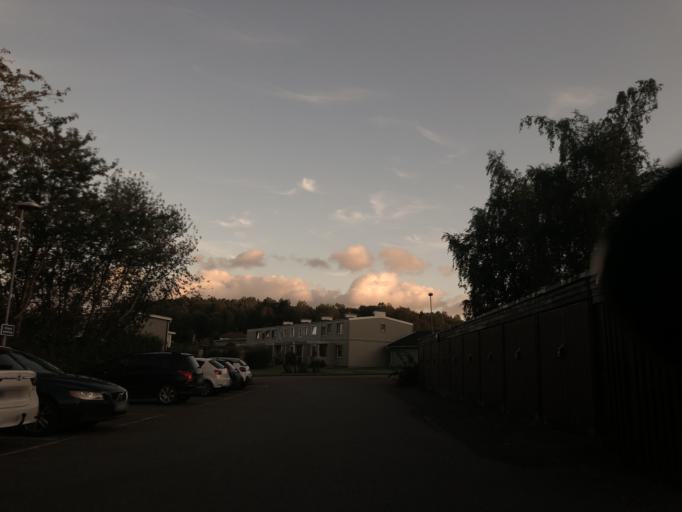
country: SE
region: Vaestra Goetaland
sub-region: Goteborg
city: Goeteborg
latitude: 57.7608
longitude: 11.9342
